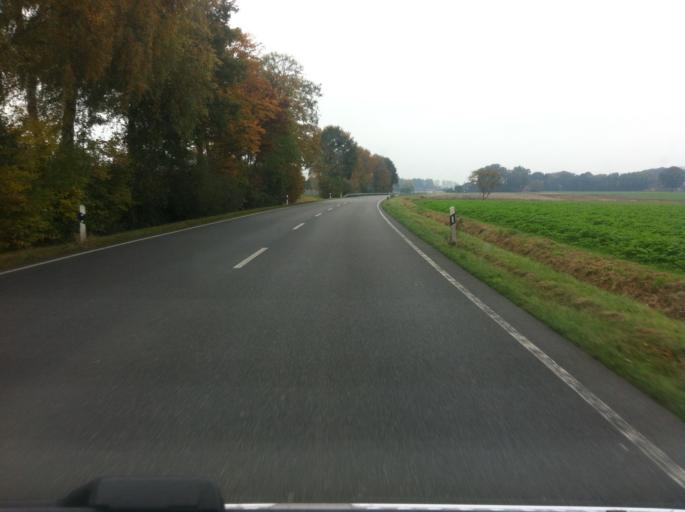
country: DE
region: North Rhine-Westphalia
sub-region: Regierungsbezirk Munster
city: Sudlohn
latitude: 51.9579
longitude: 6.8313
